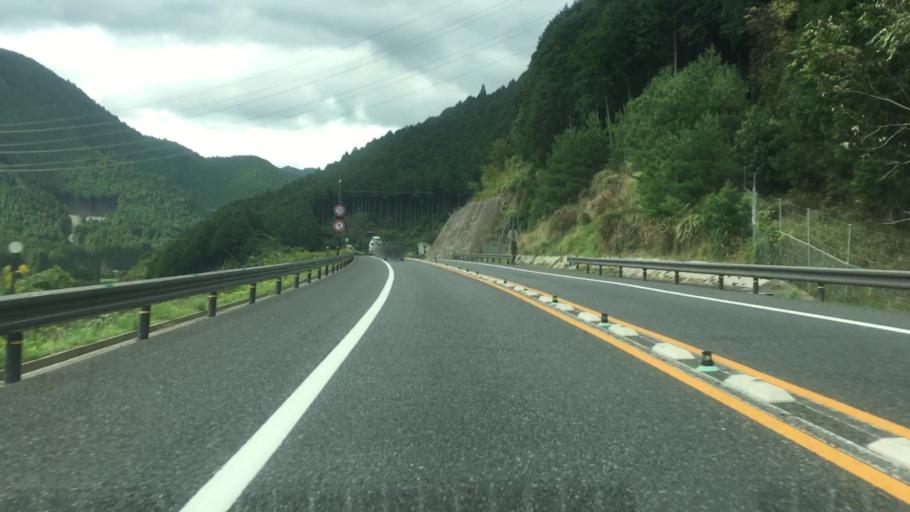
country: JP
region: Kyoto
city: Fukuchiyama
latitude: 35.2856
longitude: 134.9821
